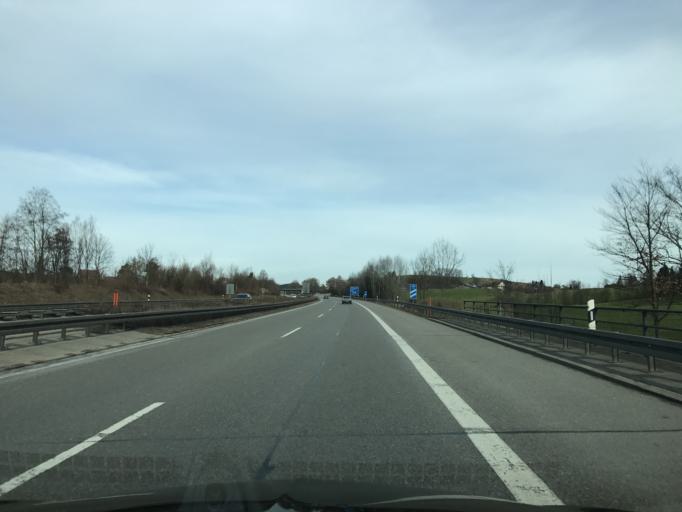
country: DE
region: Bavaria
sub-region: Swabia
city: Weissensberg
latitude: 47.5882
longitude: 9.7363
